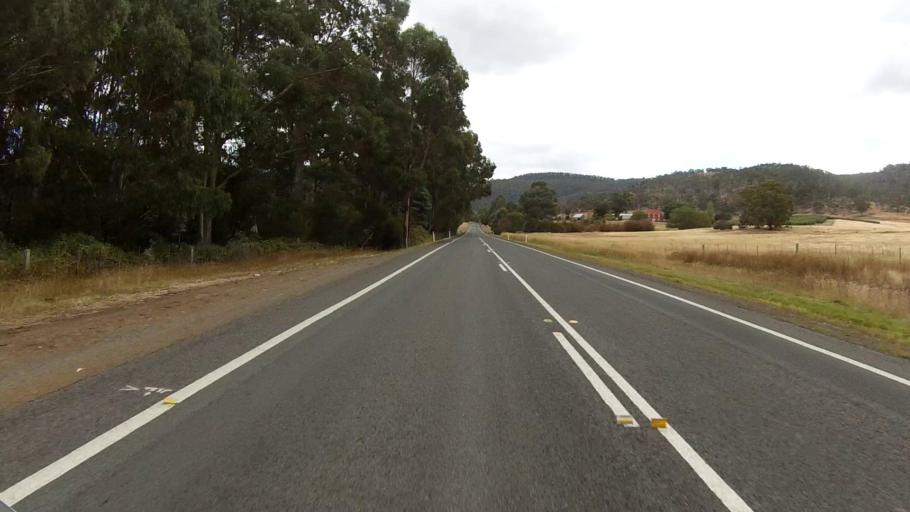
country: AU
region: Tasmania
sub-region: Sorell
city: Sorell
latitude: -42.6983
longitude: 147.5252
